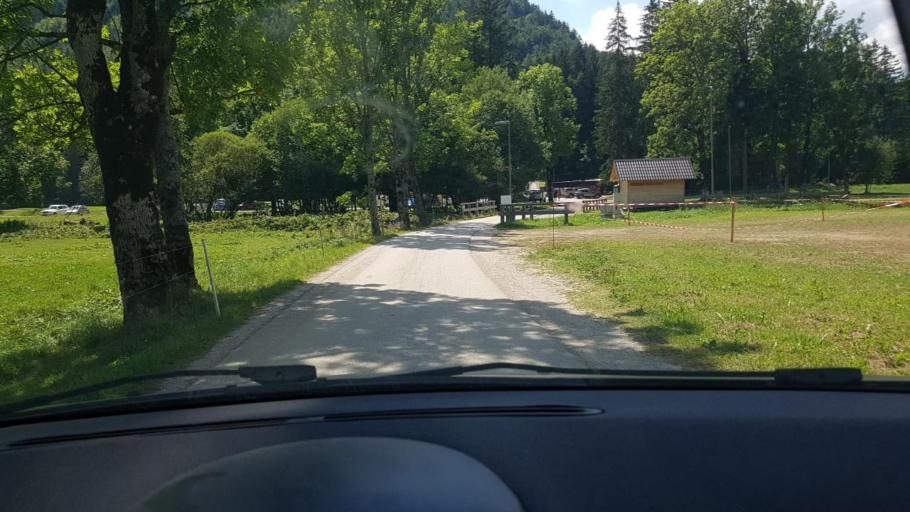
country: SI
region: Jezersko
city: Zgornje Jezersko
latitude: 46.4051
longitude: 14.5161
